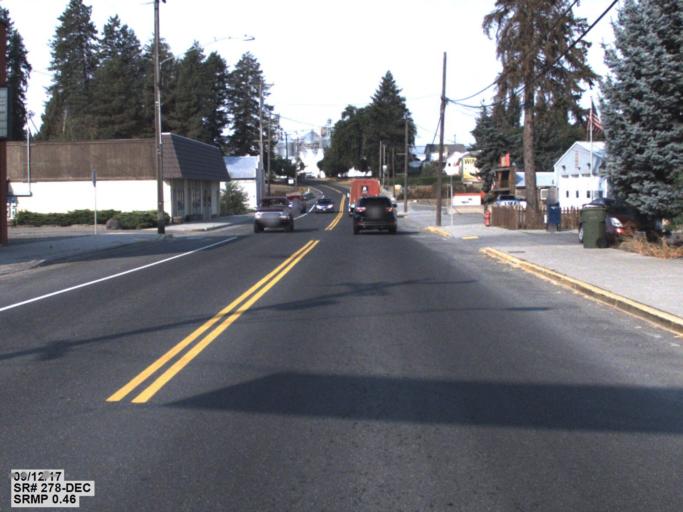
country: US
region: Washington
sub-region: Spokane County
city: Veradale
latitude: 47.4523
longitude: -117.1328
